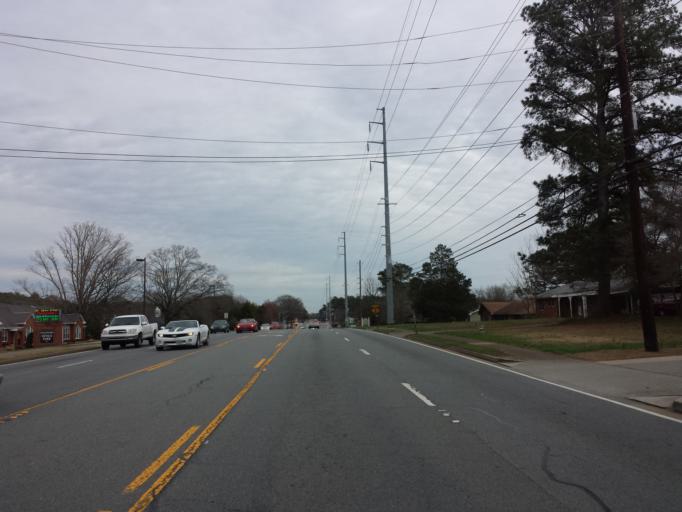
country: US
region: Georgia
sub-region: Fulton County
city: Roswell
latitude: 34.0274
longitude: -84.4274
